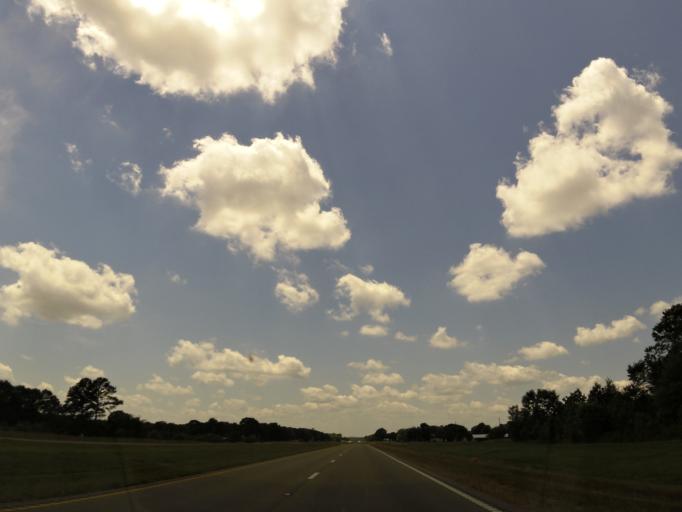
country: US
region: Mississippi
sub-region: Lee County
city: Verona
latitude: 34.2214
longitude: -88.8397
